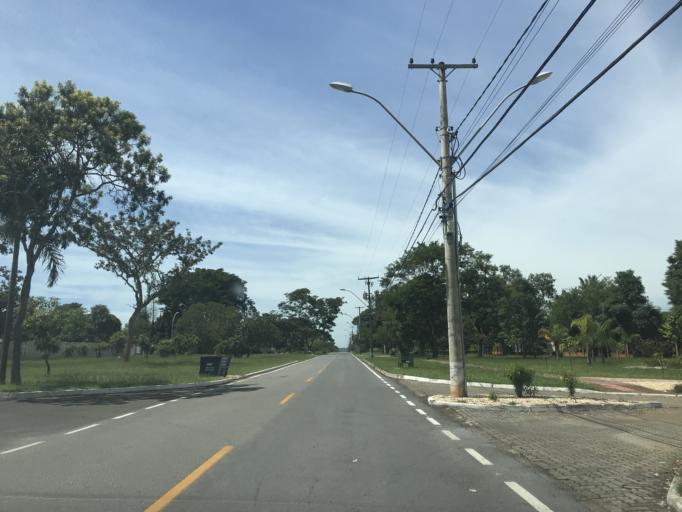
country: BR
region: Federal District
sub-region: Brasilia
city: Brasilia
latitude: -15.9016
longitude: -47.9330
